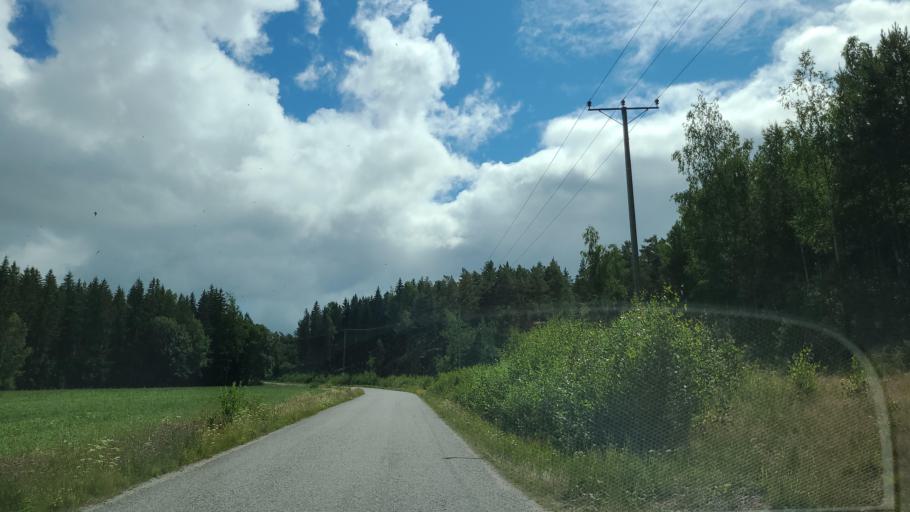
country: FI
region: Varsinais-Suomi
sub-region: Aboland-Turunmaa
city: Nagu
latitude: 60.1838
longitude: 22.0199
